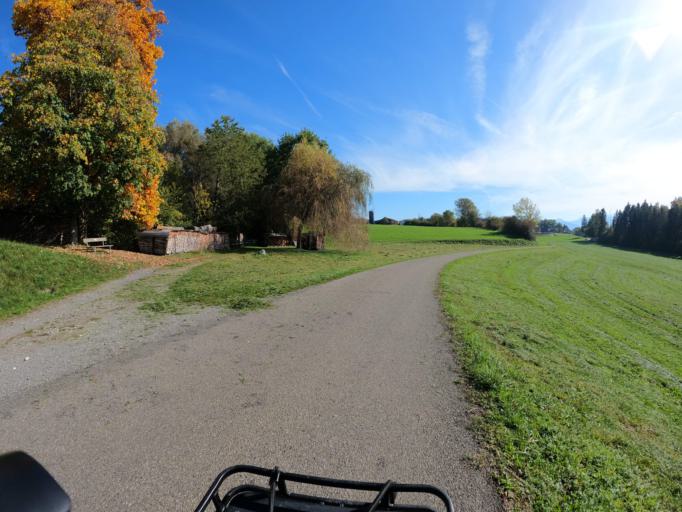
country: CH
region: Zurich
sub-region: Bezirk Affoltern
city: Mettmenstetten
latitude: 47.2413
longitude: 8.4724
